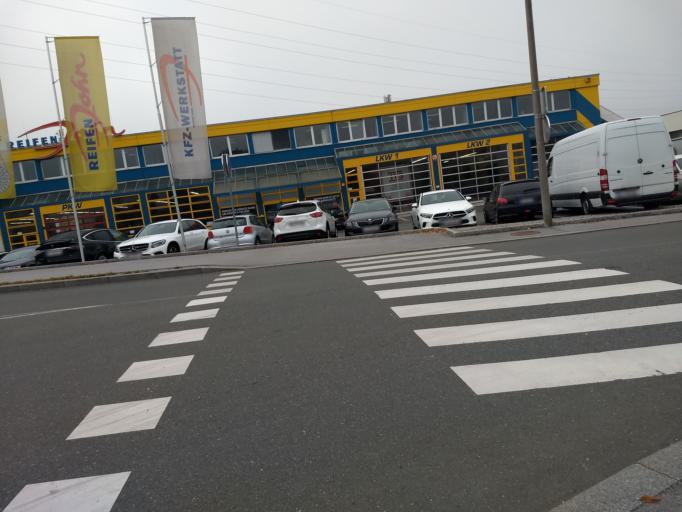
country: DE
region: Bavaria
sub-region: Upper Bavaria
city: Freilassing
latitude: 47.8304
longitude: 13.0020
